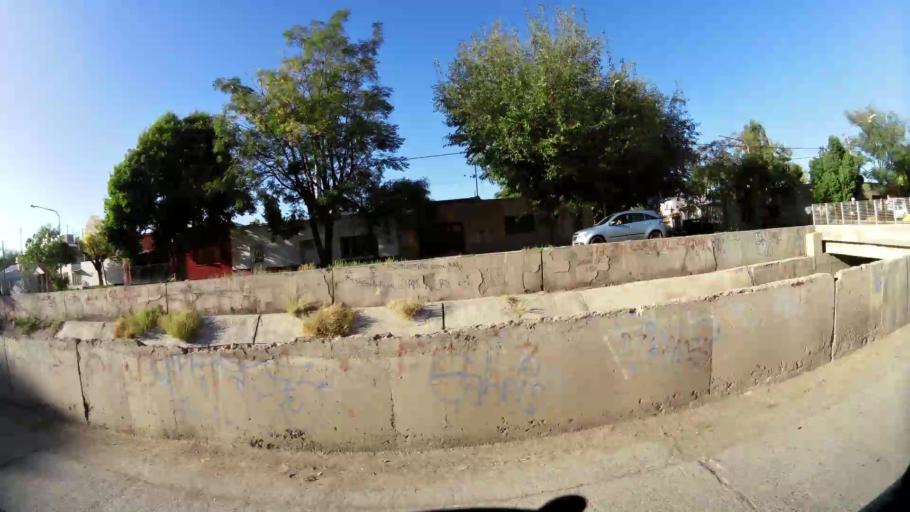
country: AR
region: Mendoza
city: Las Heras
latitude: -32.8622
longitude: -68.8257
